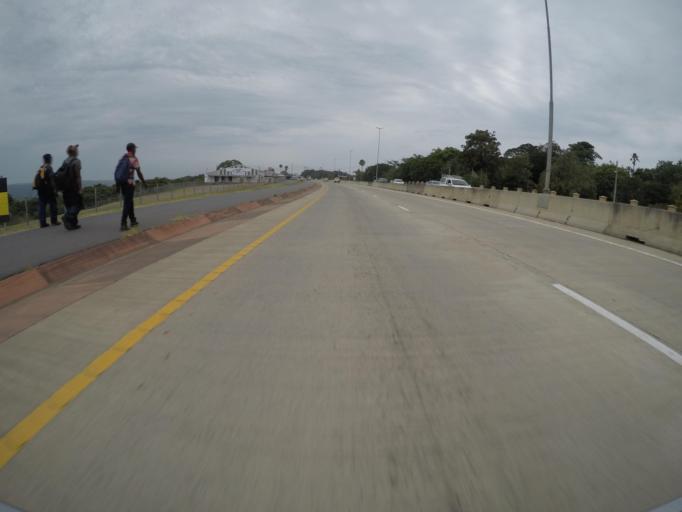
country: ZA
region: Eastern Cape
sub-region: Buffalo City Metropolitan Municipality
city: East London
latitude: -32.9426
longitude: 27.9698
